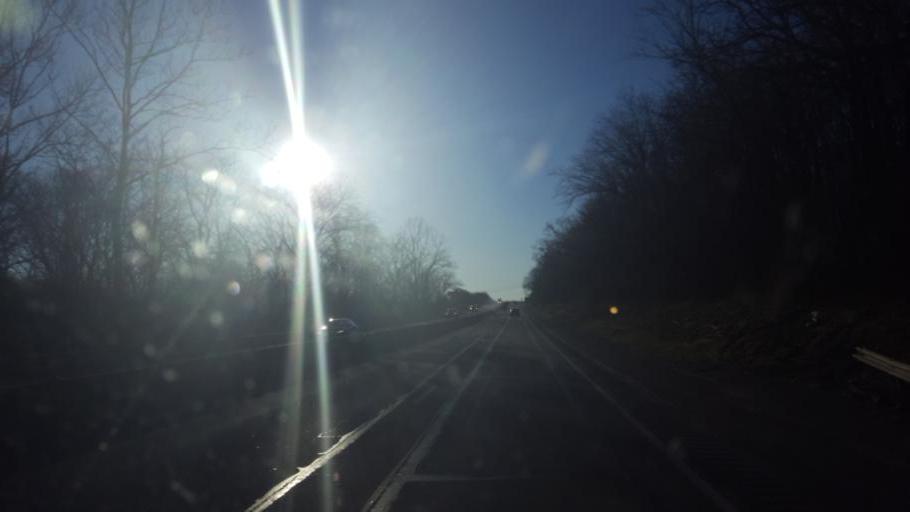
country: US
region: Pennsylvania
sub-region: Westmoreland County
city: New Stanton
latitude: 40.2110
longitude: -79.6589
